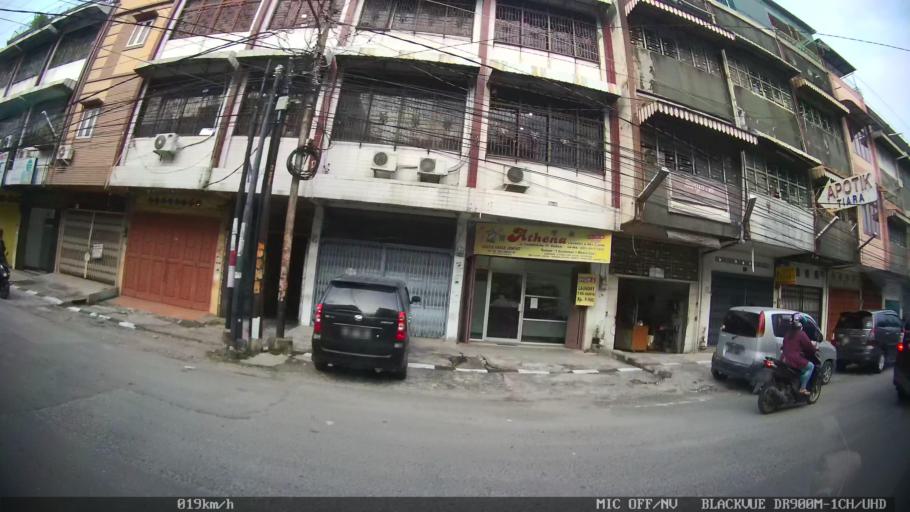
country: ID
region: North Sumatra
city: Medan
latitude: 3.5941
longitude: 98.6896
